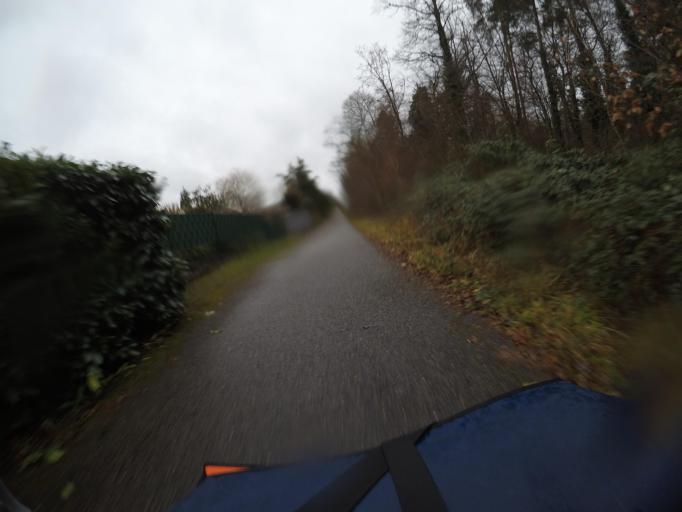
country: DE
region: Baden-Wuerttemberg
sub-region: Karlsruhe Region
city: Linkenheim-Hochstetten
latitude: 49.1016
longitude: 8.4703
